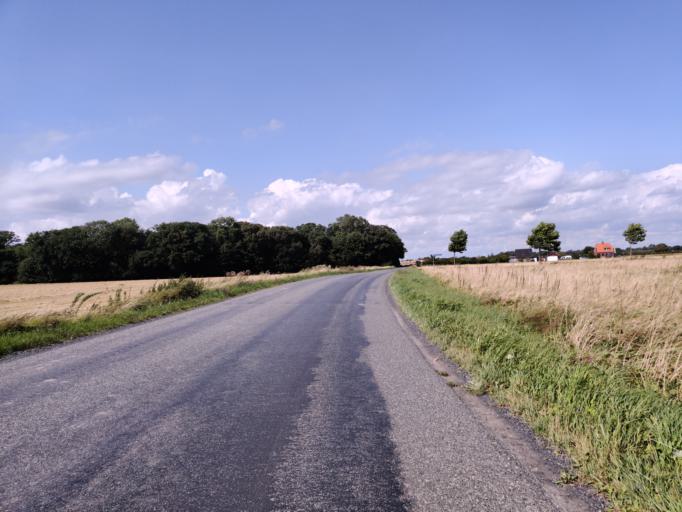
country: DK
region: Zealand
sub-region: Guldborgsund Kommune
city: Nykobing Falster
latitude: 54.6416
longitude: 11.8955
